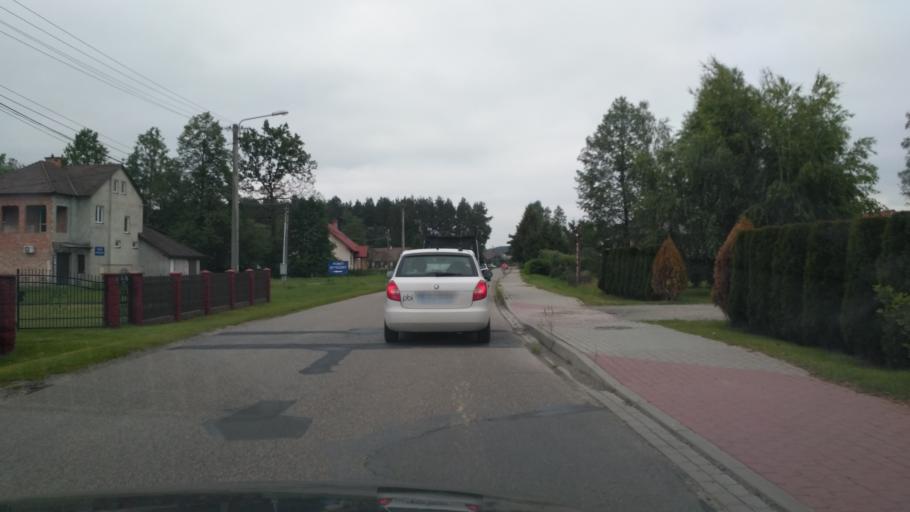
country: PL
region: Subcarpathian Voivodeship
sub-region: Powiat ropczycko-sedziszowski
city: Sedziszow Malopolski
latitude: 50.1496
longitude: 21.6702
